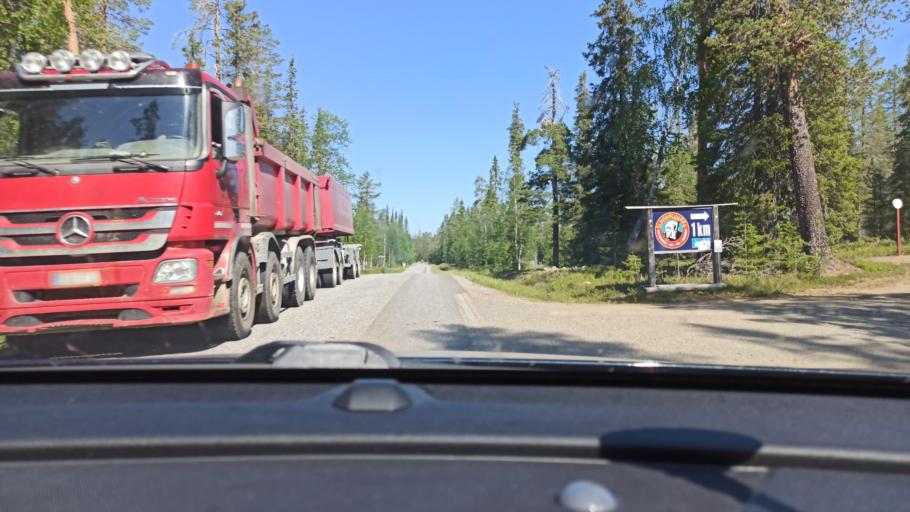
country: FI
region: Lapland
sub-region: Tunturi-Lappi
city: Kolari
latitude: 67.6653
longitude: 24.1615
